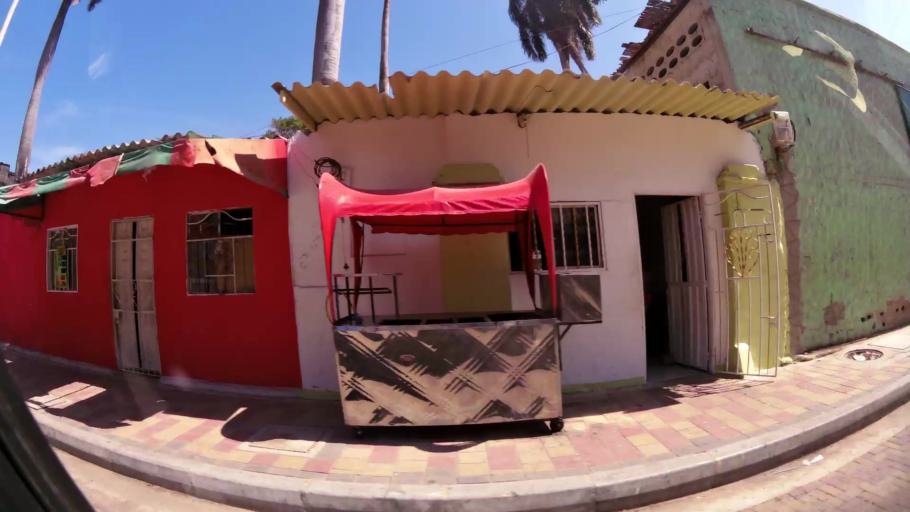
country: CO
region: Atlantico
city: Barranquilla
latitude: 10.9730
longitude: -74.7803
